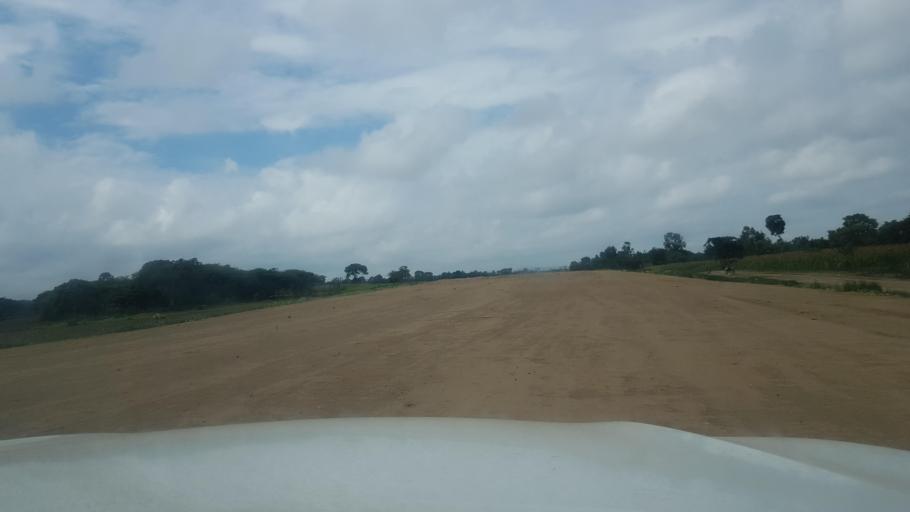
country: ET
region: Oromiya
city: Shashemene
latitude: 7.2668
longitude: 38.5975
